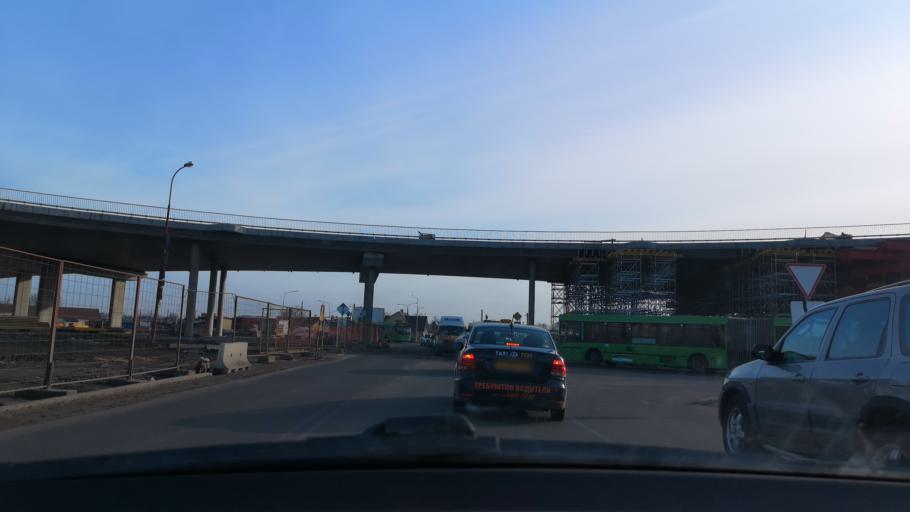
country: BY
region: Brest
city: Brest
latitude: 52.1052
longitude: 23.6656
